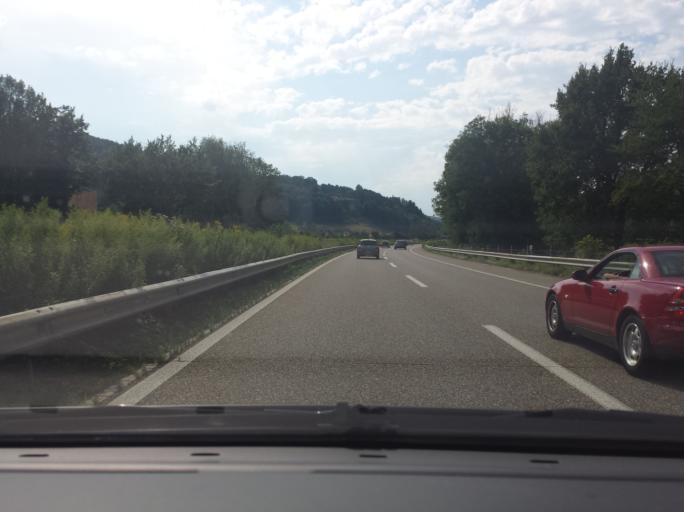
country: CH
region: Saint Gallen
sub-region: Wahlkreis Rheintal
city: Sankt Margrethen
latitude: 47.4563
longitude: 9.6271
